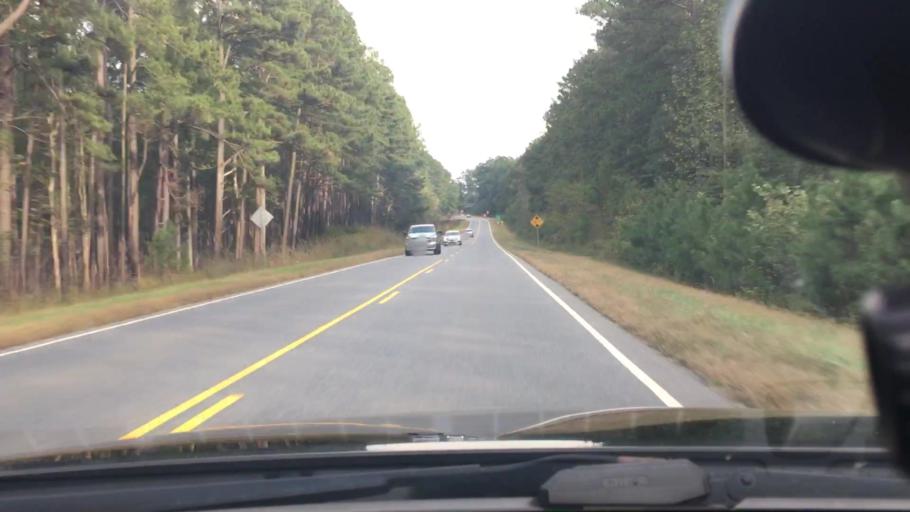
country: US
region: North Carolina
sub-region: Montgomery County
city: Troy
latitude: 35.3221
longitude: -79.9518
